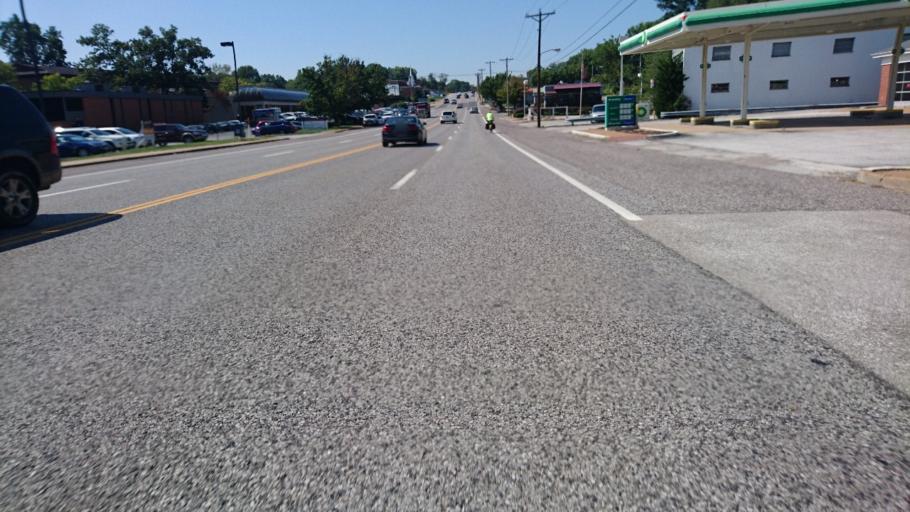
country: US
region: Missouri
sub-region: Saint Louis County
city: Kirkwood
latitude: 38.5998
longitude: -90.4090
